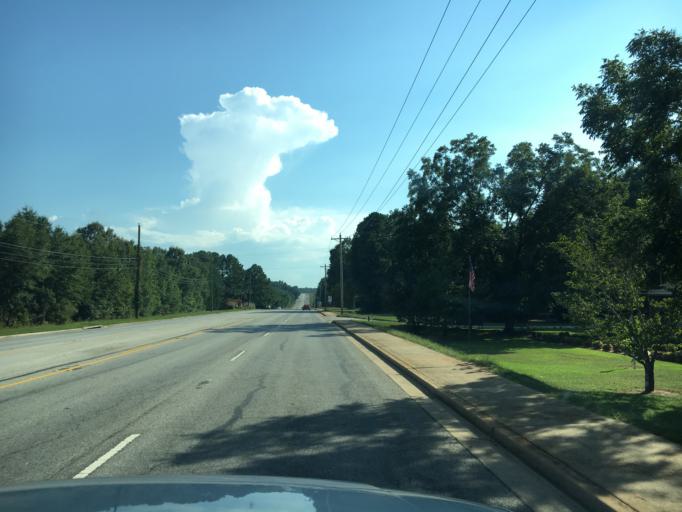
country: US
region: South Carolina
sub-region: Laurens County
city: Clinton
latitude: 34.4485
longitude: -81.8857
